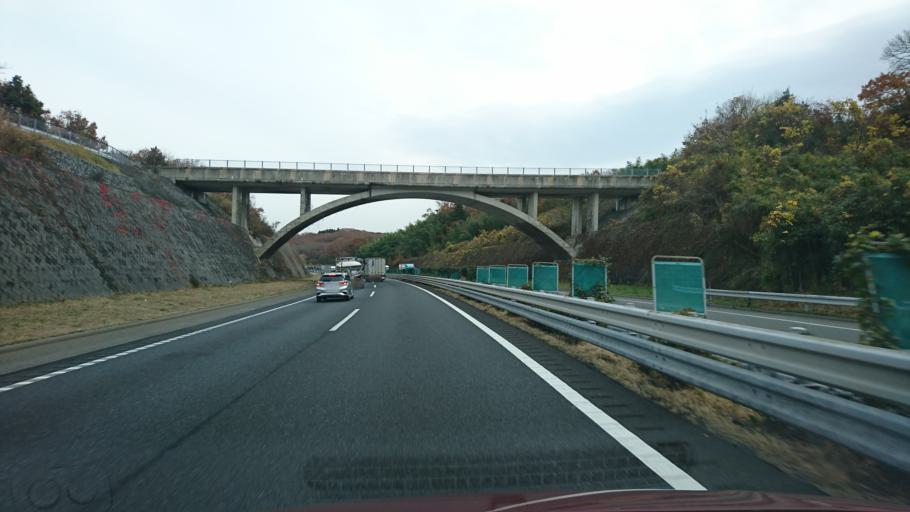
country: JP
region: Hyogo
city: Sandacho
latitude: 34.8275
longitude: 135.1808
